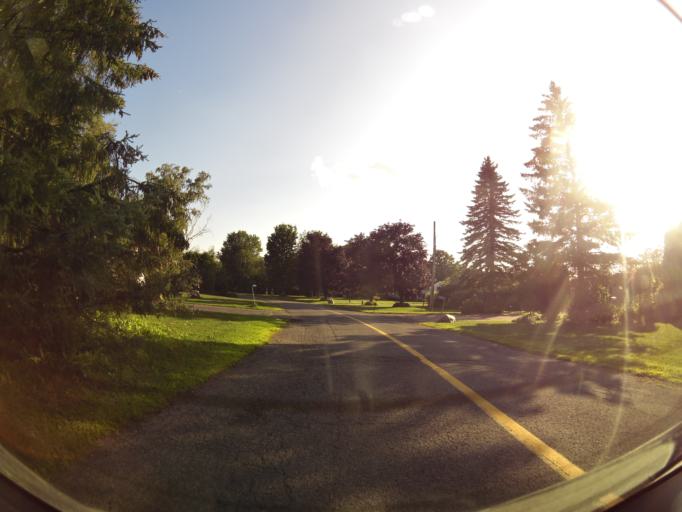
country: CA
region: Ontario
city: Clarence-Rockland
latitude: 45.5120
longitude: -75.4605
